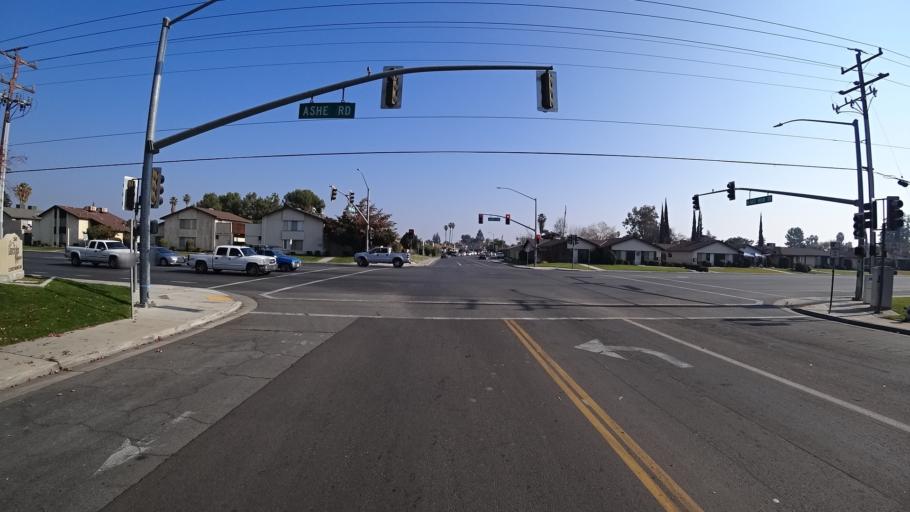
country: US
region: California
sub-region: Kern County
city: Greenacres
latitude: 35.3302
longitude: -119.0748
